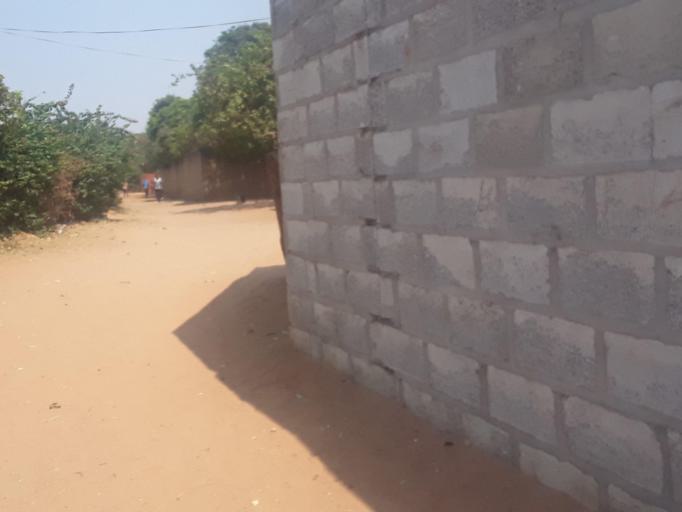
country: ZM
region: Lusaka
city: Lusaka
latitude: -15.3557
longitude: 28.2975
